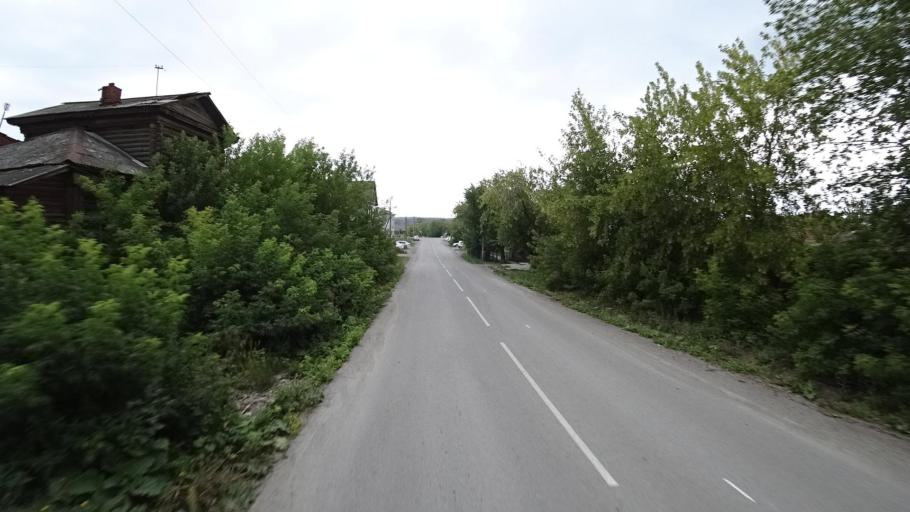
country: RU
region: Sverdlovsk
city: Kamyshlov
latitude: 56.8463
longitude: 62.6952
